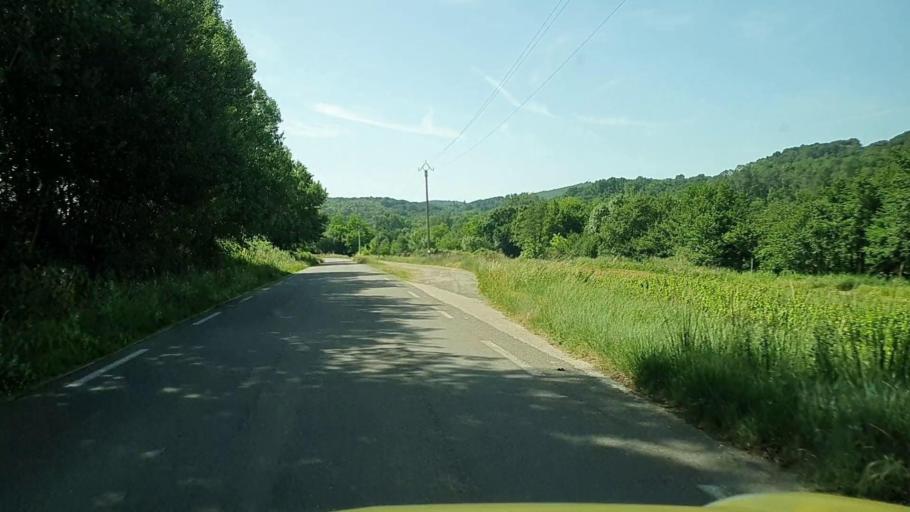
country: FR
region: Languedoc-Roussillon
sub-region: Departement du Gard
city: Tresques
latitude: 44.1004
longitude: 4.5464
